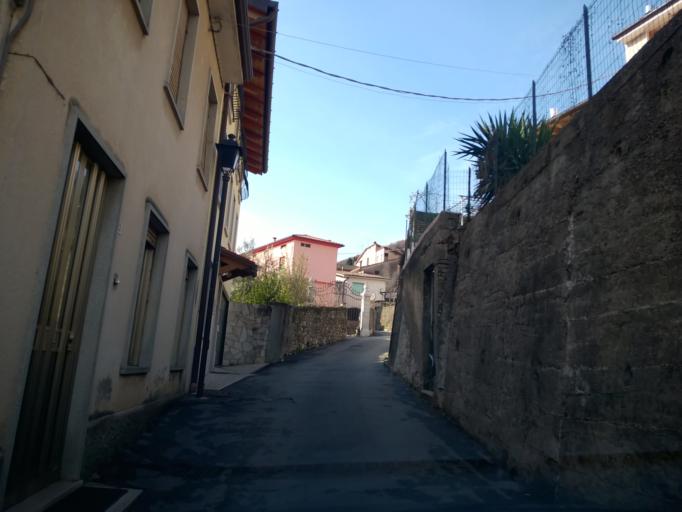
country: IT
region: Veneto
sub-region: Provincia di Vicenza
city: Piovene Rocchette
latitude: 45.7599
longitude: 11.4291
